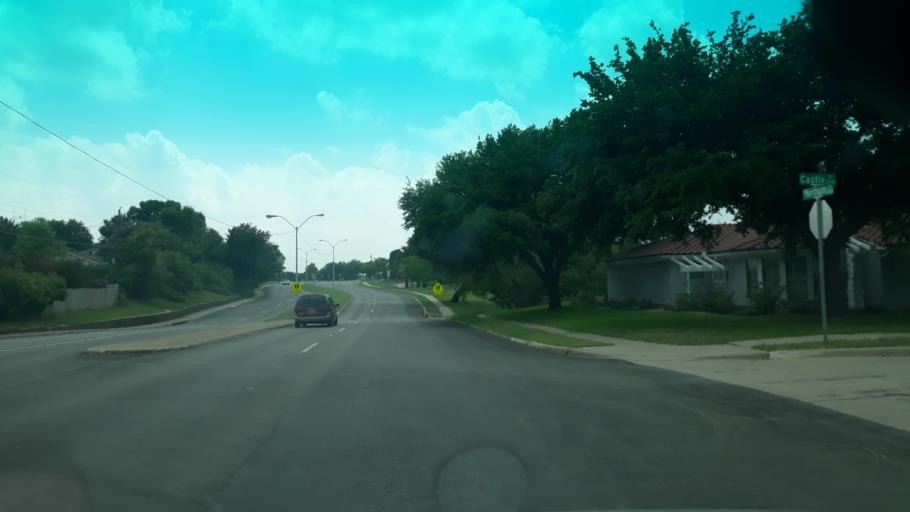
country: US
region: Texas
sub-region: Dallas County
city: Irving
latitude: 32.8563
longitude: -96.9830
